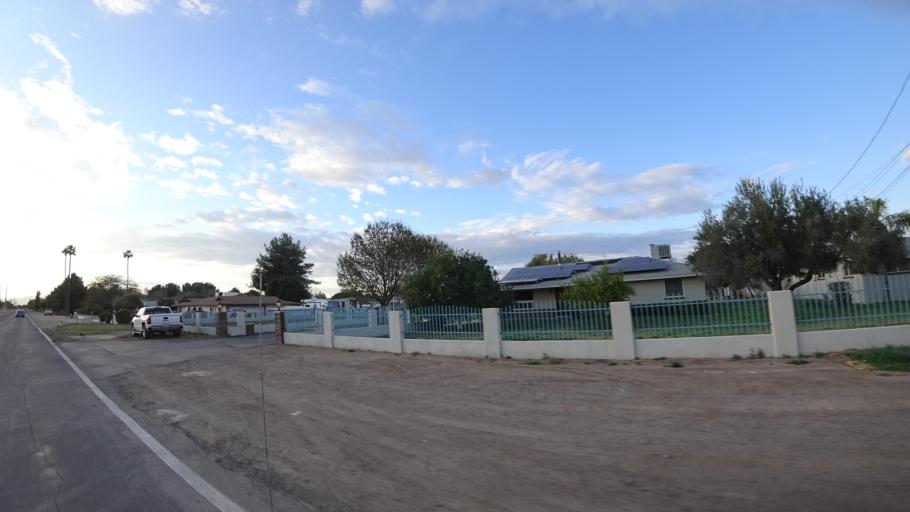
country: US
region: Arizona
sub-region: Maricopa County
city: Peoria
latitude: 33.5451
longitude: -112.2242
